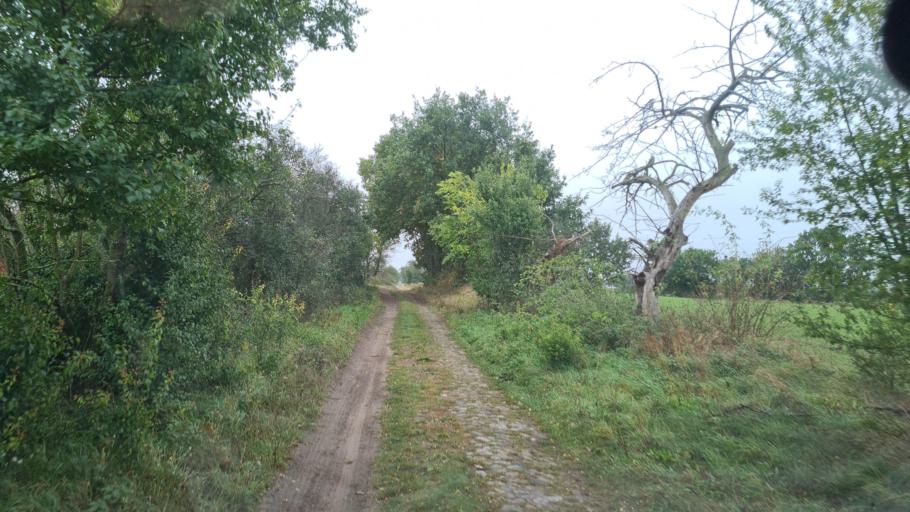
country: DE
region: Brandenburg
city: Furstenwalde
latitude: 52.4129
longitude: 14.0329
